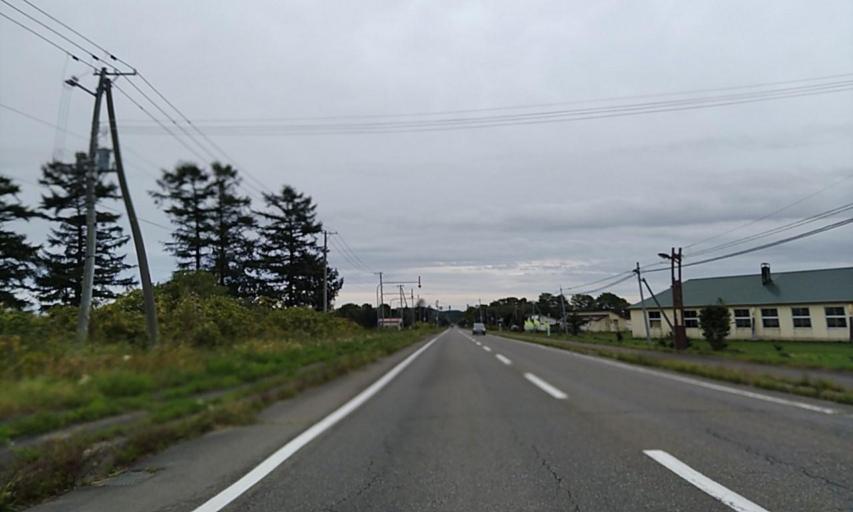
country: JP
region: Hokkaido
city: Obihiro
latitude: 42.4560
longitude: 143.2872
